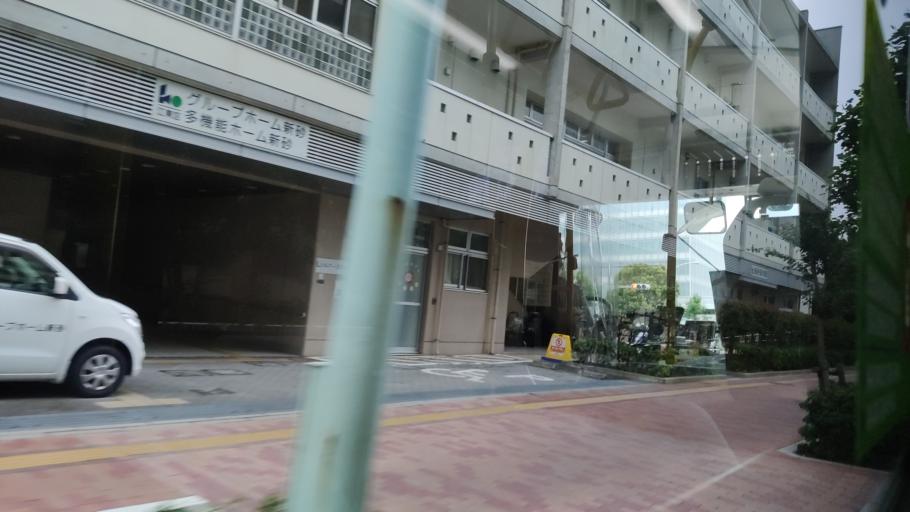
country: JP
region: Tokyo
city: Urayasu
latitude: 35.6667
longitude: 139.8332
